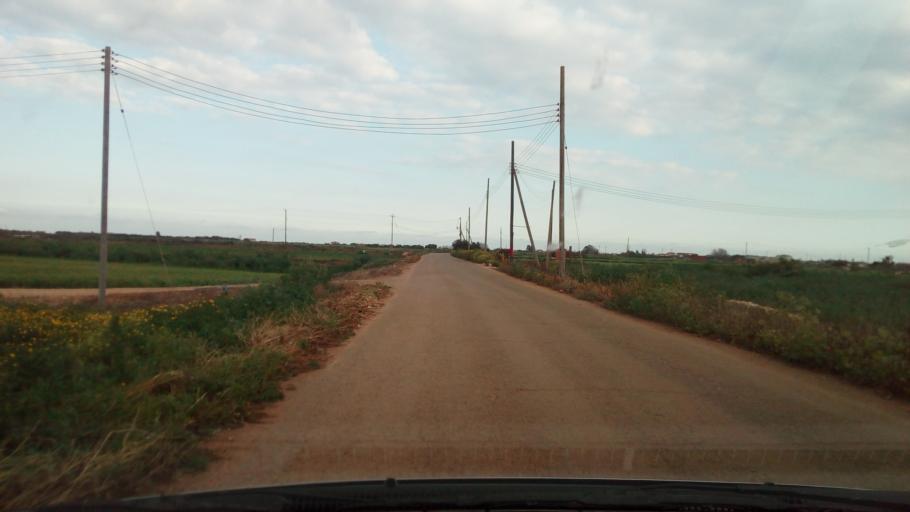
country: CY
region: Ammochostos
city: Avgorou
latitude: 34.9939
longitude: 33.8255
